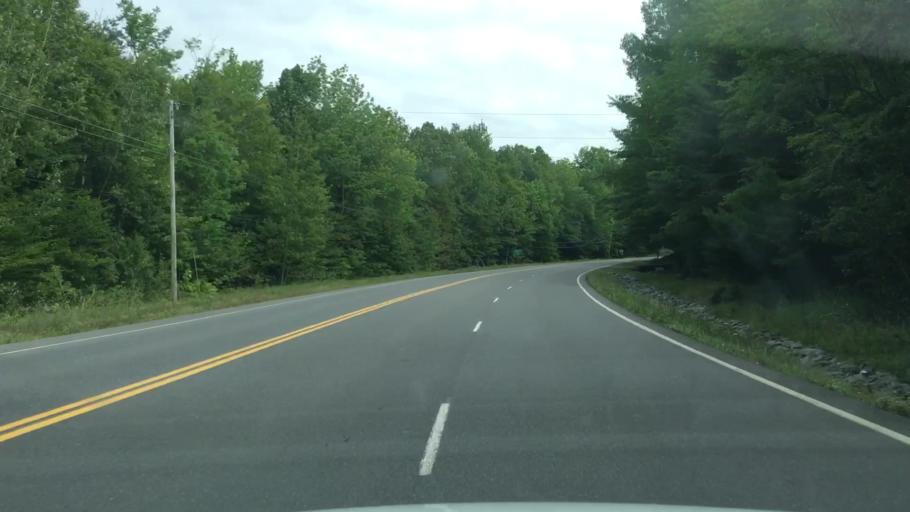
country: US
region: Maine
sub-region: Piscataquis County
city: Dover-Foxcroft
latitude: 45.2141
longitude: -69.1687
